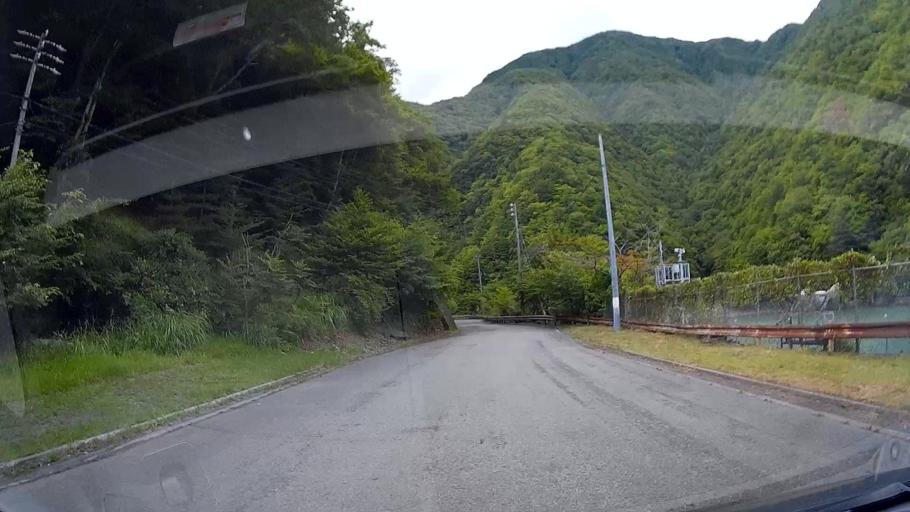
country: JP
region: Shizuoka
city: Shizuoka-shi
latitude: 35.3083
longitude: 138.2019
